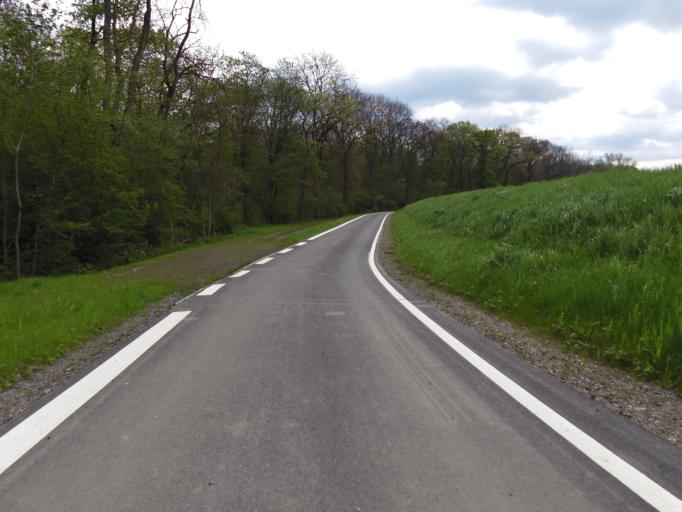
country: DE
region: Rheinland-Pfalz
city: Eich
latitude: 49.7047
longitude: 8.3930
